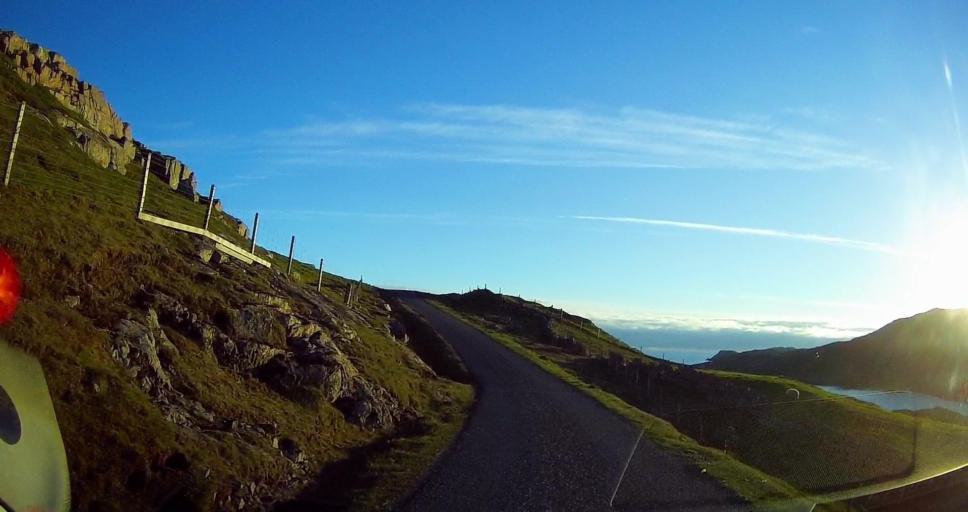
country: GB
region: Scotland
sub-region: Shetland Islands
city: Lerwick
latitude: 60.4491
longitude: -1.4250
